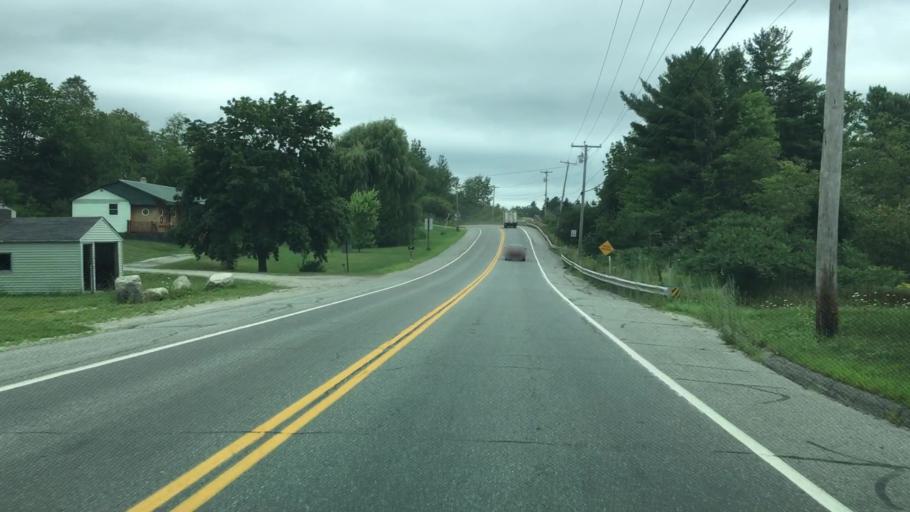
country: US
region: Maine
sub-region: Waldo County
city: Frankfort
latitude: 44.5539
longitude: -68.8644
